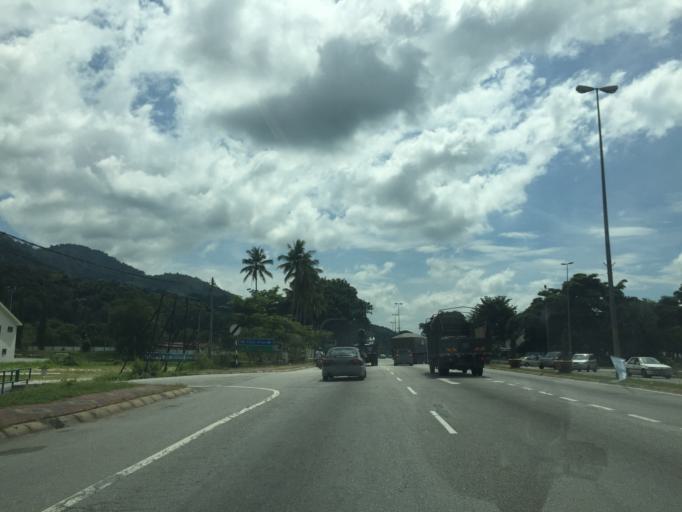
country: MY
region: Perak
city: Kampar
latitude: 4.3014
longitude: 101.1585
